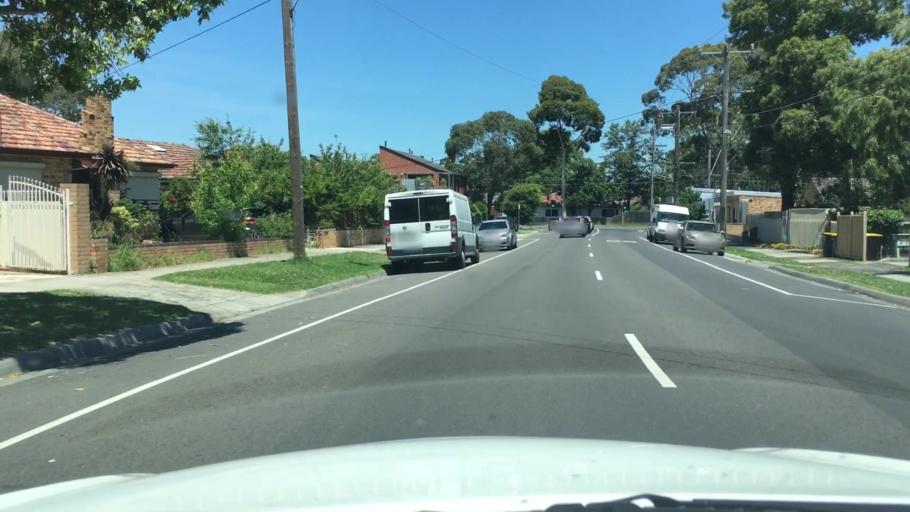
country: AU
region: Victoria
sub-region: Greater Dandenong
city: Noble Park
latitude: -37.9647
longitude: 145.1787
